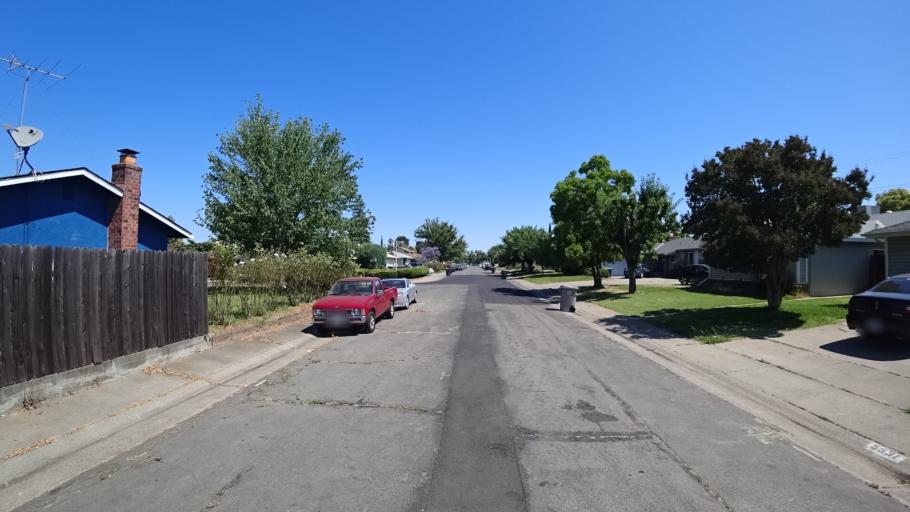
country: US
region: California
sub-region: Sacramento County
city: Florin
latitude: 38.5261
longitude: -121.4110
